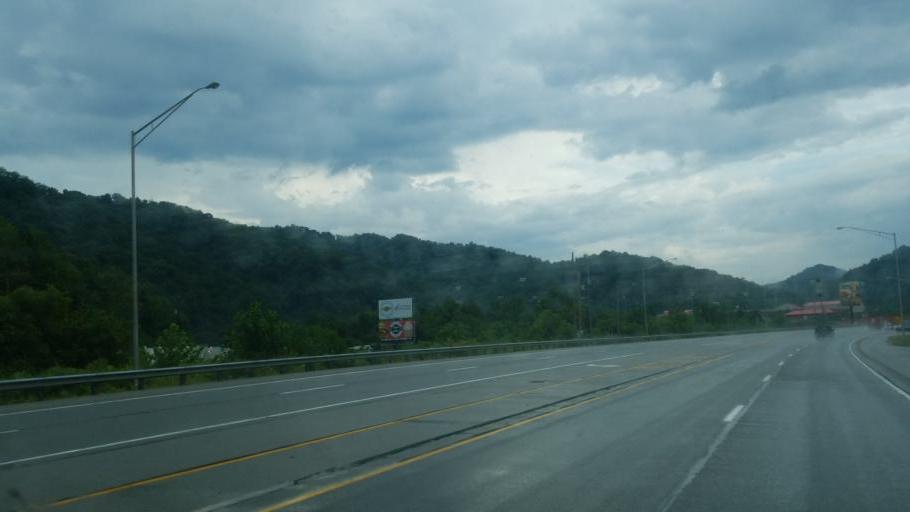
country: US
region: West Virginia
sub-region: Mingo County
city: Williamson
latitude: 37.6536
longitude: -82.2690
